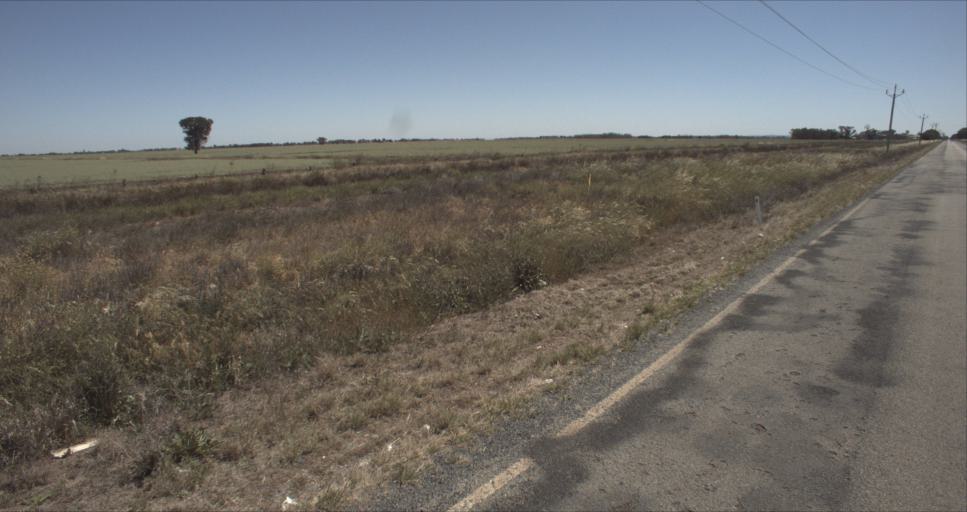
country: AU
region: New South Wales
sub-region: Leeton
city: Leeton
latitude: -34.5093
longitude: 146.2854
